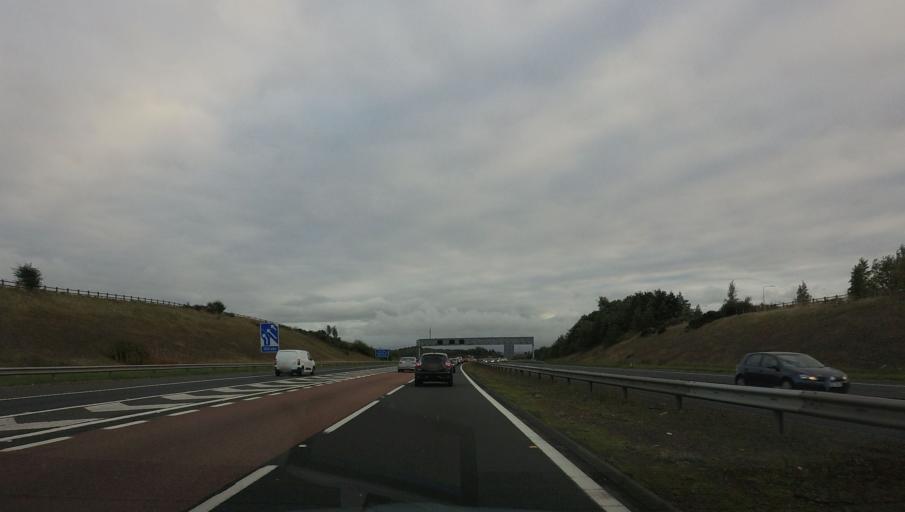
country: GB
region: Scotland
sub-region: Fife
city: Crossgates
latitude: 56.0718
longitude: -3.3885
